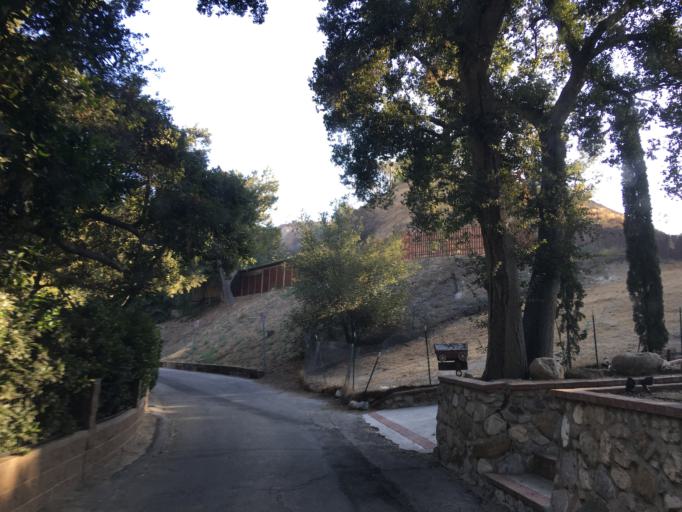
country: US
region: California
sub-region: Los Angeles County
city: San Fernando
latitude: 34.2888
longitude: -118.3754
